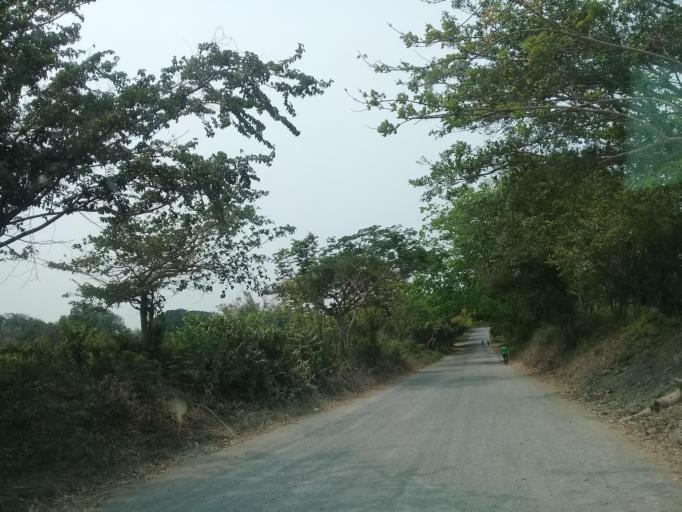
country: MX
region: Veracruz
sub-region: Medellin
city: La Laguna y Monte del Castillo
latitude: 18.9458
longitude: -96.1263
